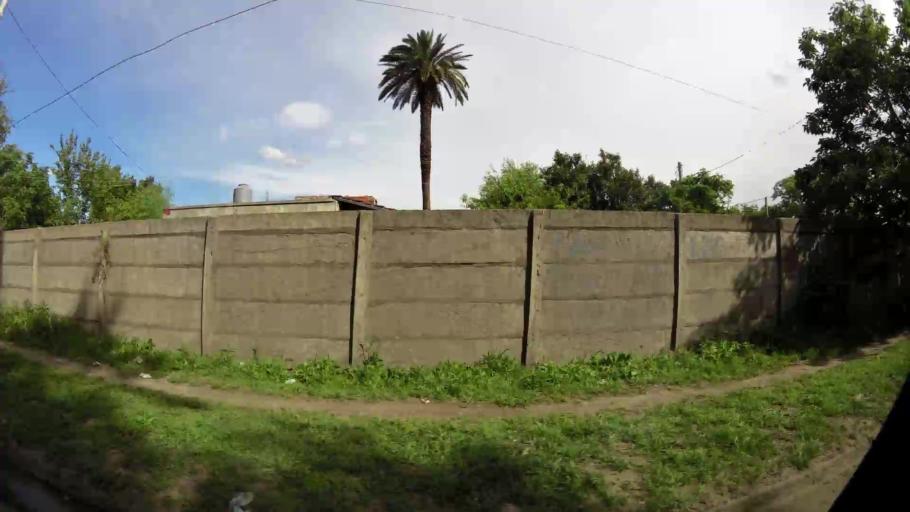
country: AR
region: Buenos Aires
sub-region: Partido de Almirante Brown
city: Adrogue
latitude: -34.8116
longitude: -58.3484
